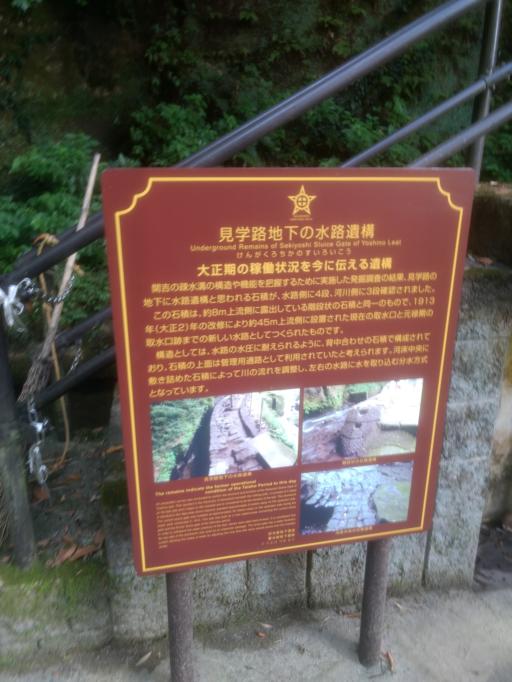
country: JP
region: Kagoshima
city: Kagoshima-shi
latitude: 31.6470
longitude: 130.5526
